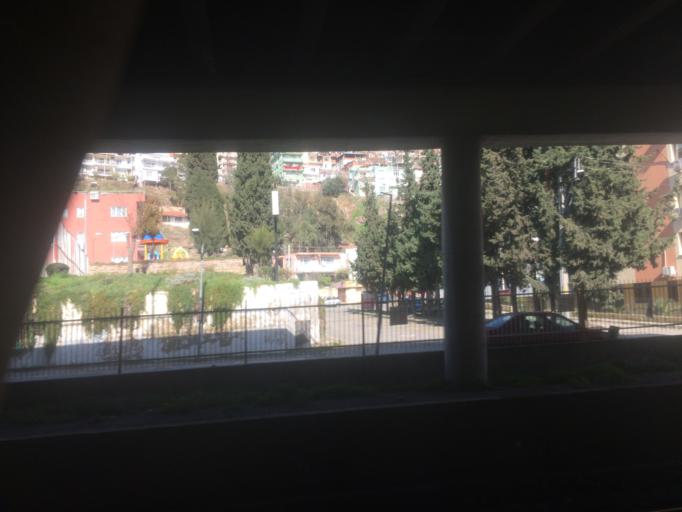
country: TR
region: Izmir
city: Karsiyaka
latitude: 38.4686
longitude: 27.1567
